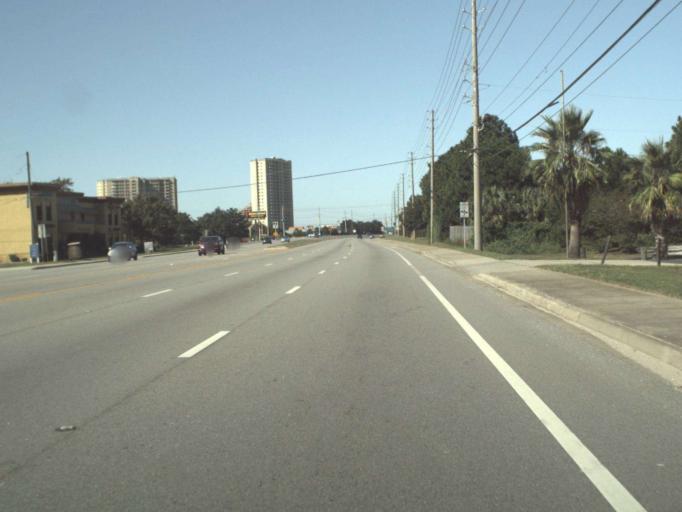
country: US
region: Florida
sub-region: Walton County
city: Miramar Beach
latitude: 30.3771
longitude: -86.3420
